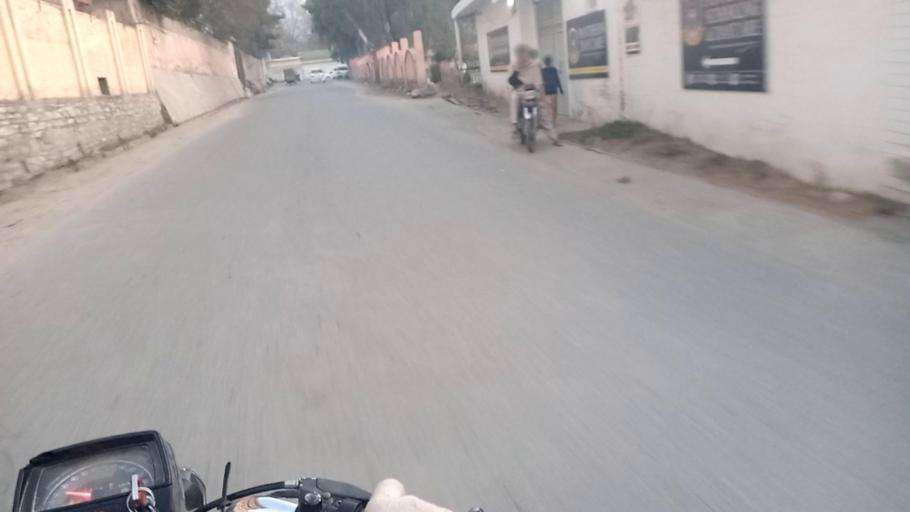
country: PK
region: Khyber Pakhtunkhwa
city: Saidu Sharif
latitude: 34.7614
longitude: 72.3599
